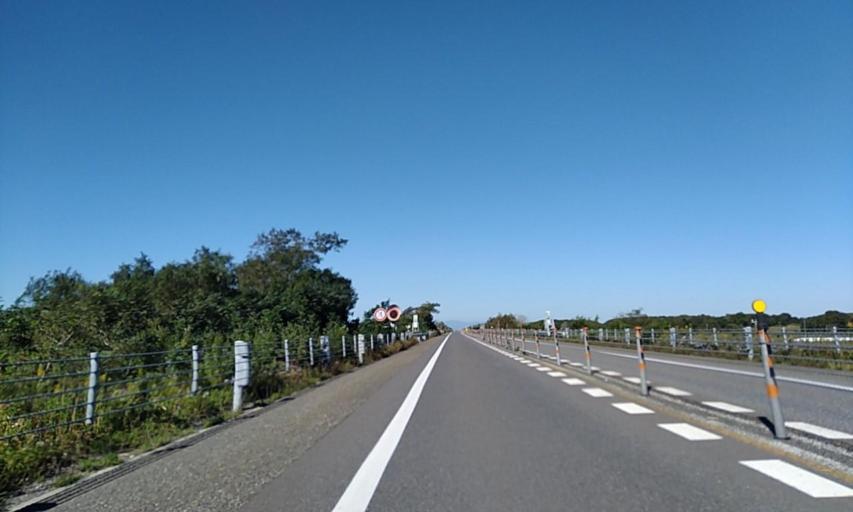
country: JP
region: Hokkaido
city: Tomakomai
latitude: 42.6072
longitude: 141.8694
